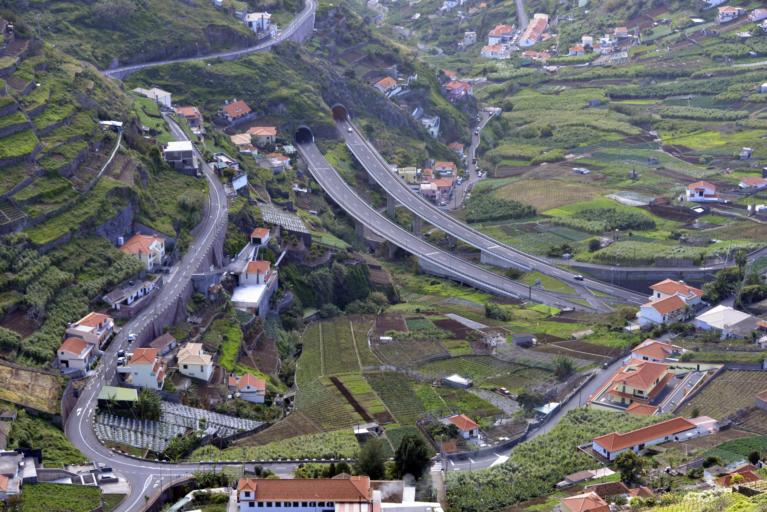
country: PT
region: Madeira
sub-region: Ribeira Brava
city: Campanario
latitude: 32.6648
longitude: -17.0025
